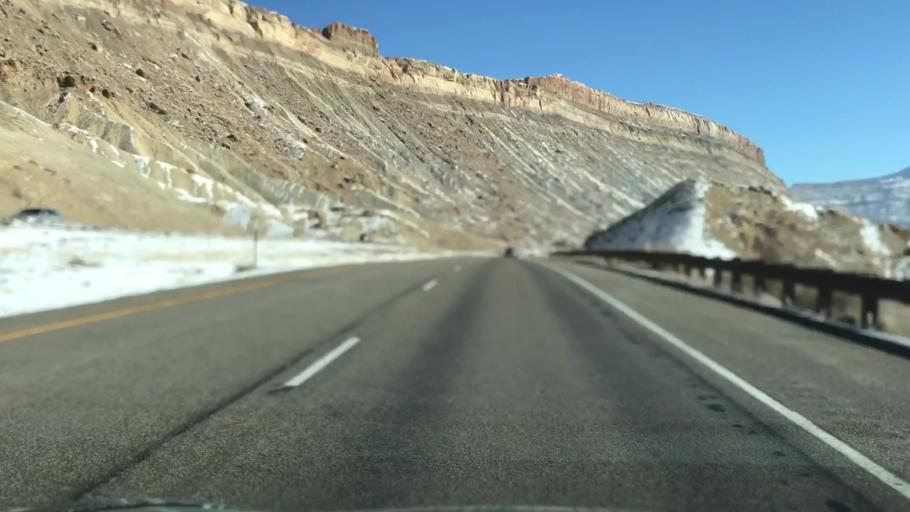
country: US
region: Colorado
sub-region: Mesa County
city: Palisade
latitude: 39.1198
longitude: -108.3781
